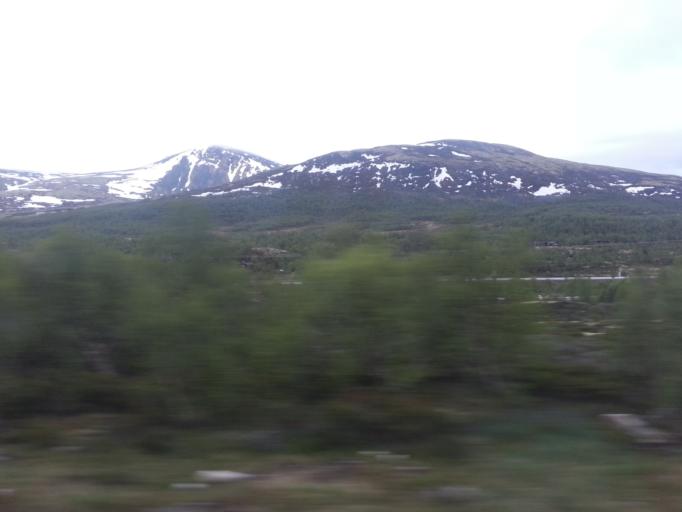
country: NO
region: Oppland
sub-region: Dovre
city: Dovre
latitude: 62.1756
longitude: 9.4344
